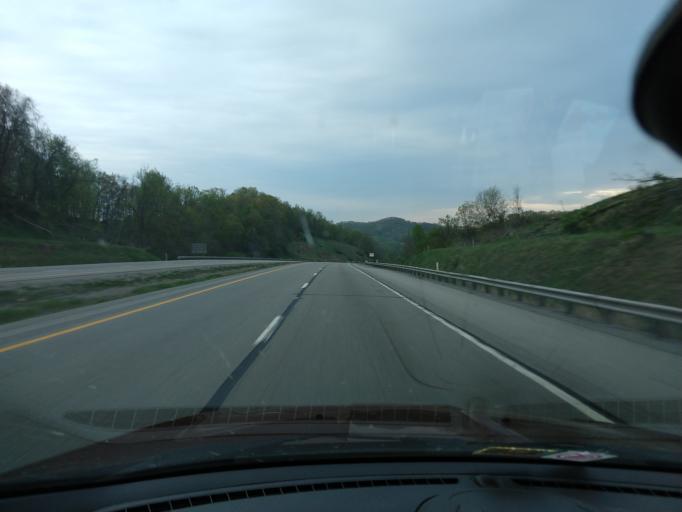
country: US
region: West Virginia
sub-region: Lewis County
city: Weston
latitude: 38.9158
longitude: -80.5727
